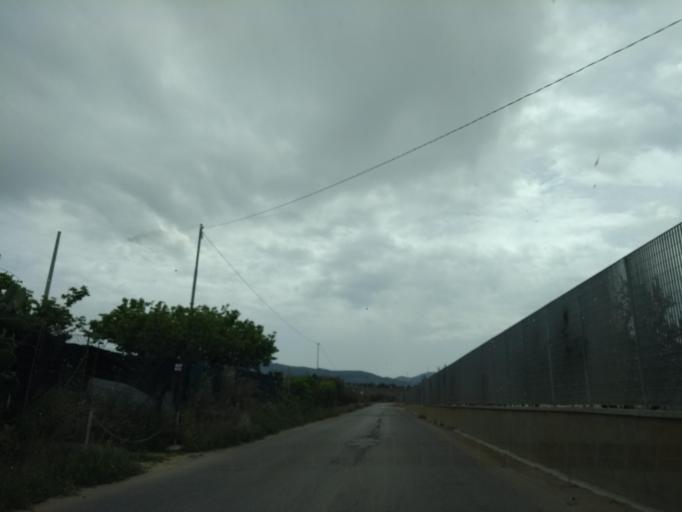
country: IT
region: Sicily
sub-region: Palermo
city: Partinico
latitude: 38.0037
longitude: 13.0682
